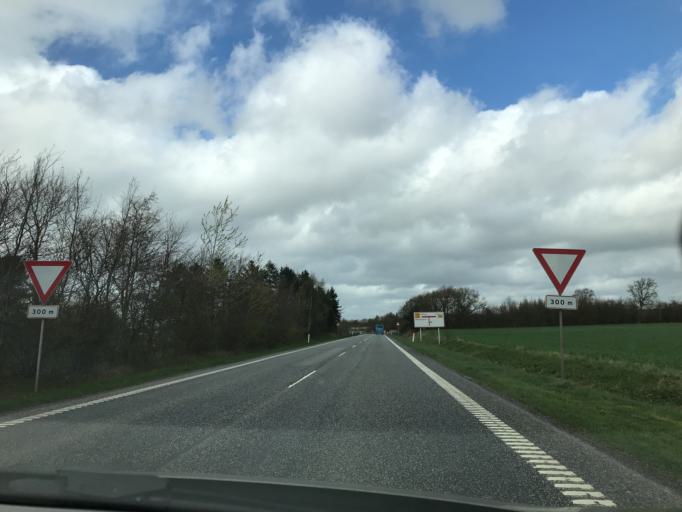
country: DK
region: Central Jutland
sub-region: Viborg Kommune
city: Stoholm
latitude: 56.4031
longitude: 9.0028
